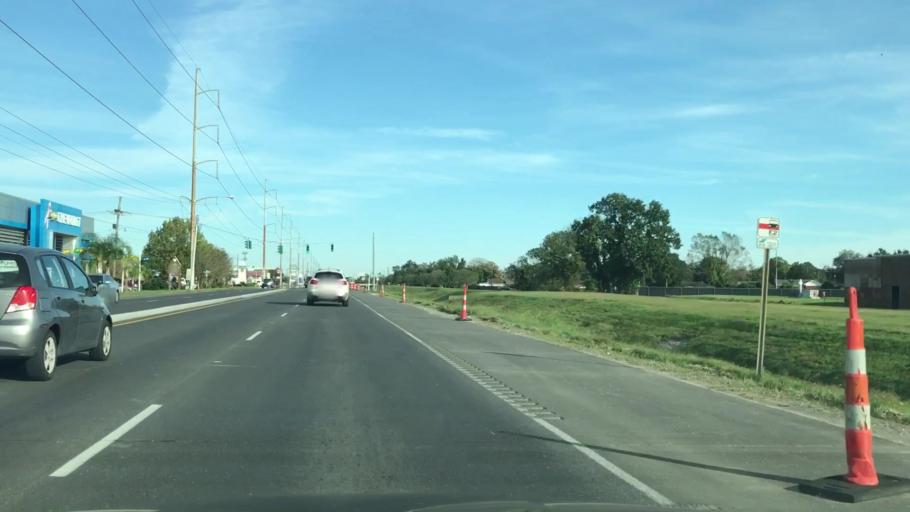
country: US
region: Louisiana
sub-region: Jefferson Parish
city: Kenner
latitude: 29.9788
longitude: -90.2277
